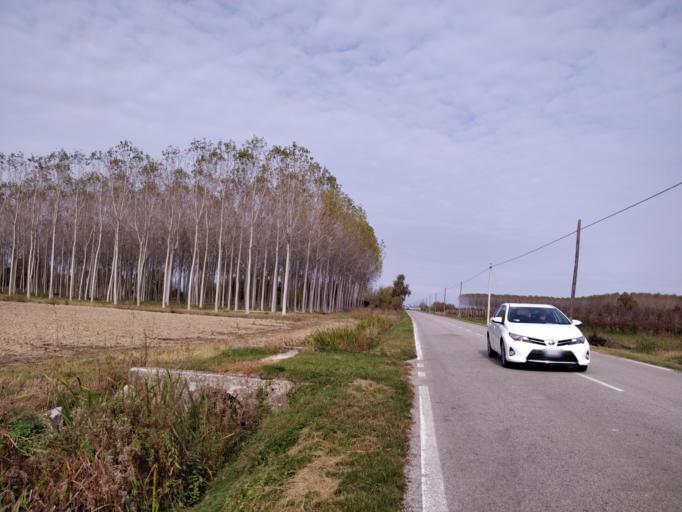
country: IT
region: Friuli Venezia Giulia
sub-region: Provincia di Udine
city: Bertiolo
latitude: 45.9241
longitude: 13.0484
